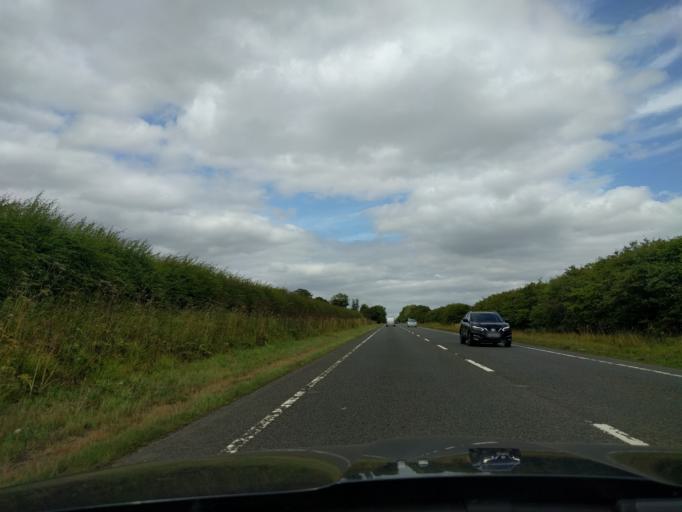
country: GB
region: England
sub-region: Northumberland
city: Alnwick
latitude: 55.4413
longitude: -1.6969
